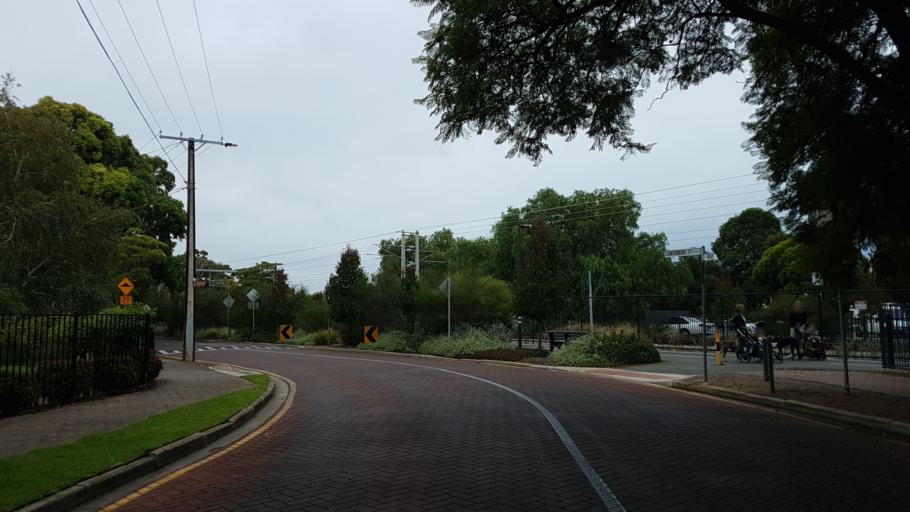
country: AU
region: South Australia
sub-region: Unley
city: Millswood
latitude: -34.9625
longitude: 138.5785
